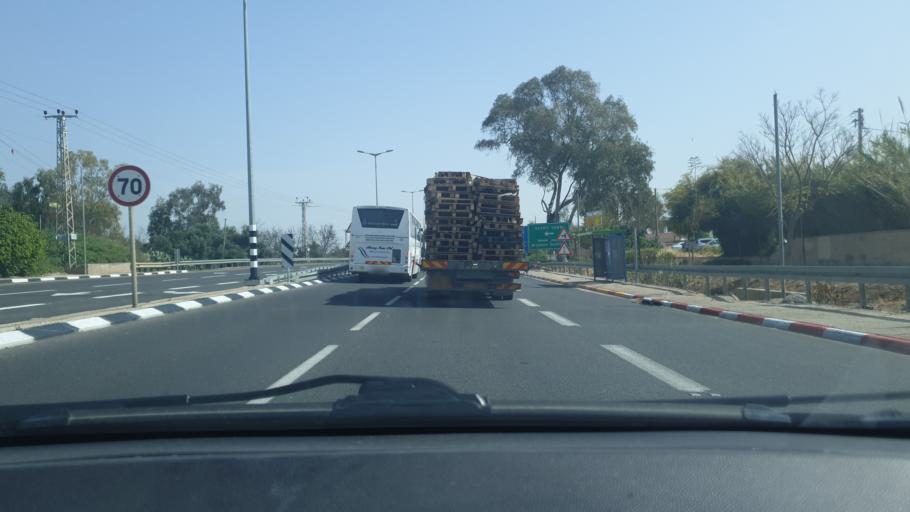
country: IL
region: Central District
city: Bet Dagan
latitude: 32.0040
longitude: 34.8261
